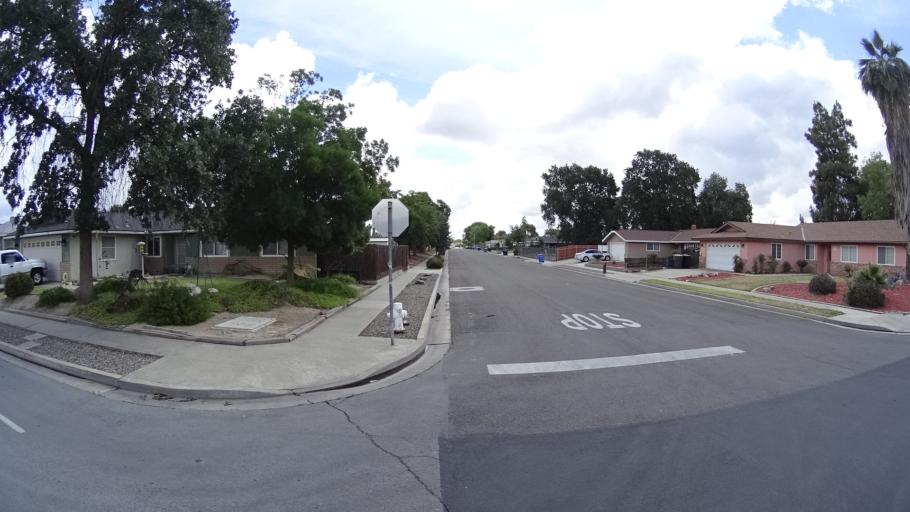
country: US
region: California
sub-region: Kings County
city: Hanford
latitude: 36.3396
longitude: -119.6657
